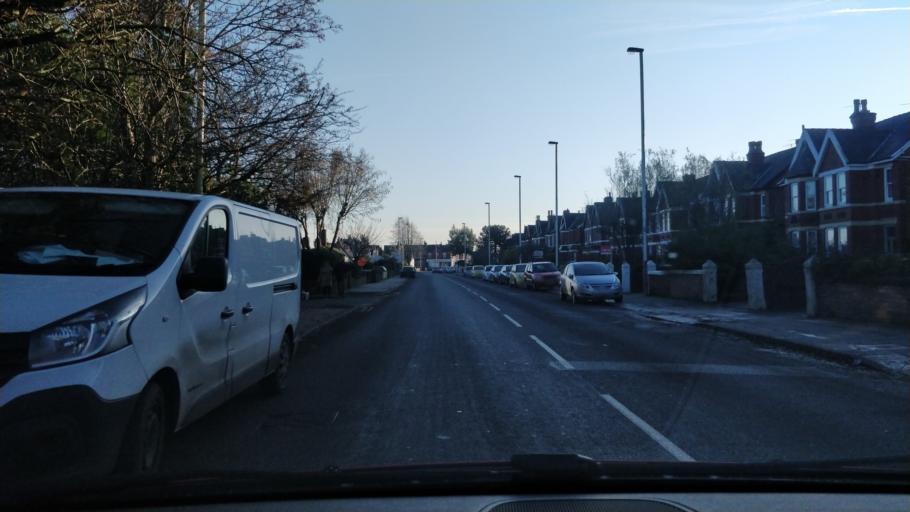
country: GB
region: England
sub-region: Sefton
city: Southport
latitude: 53.6564
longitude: -2.9658
